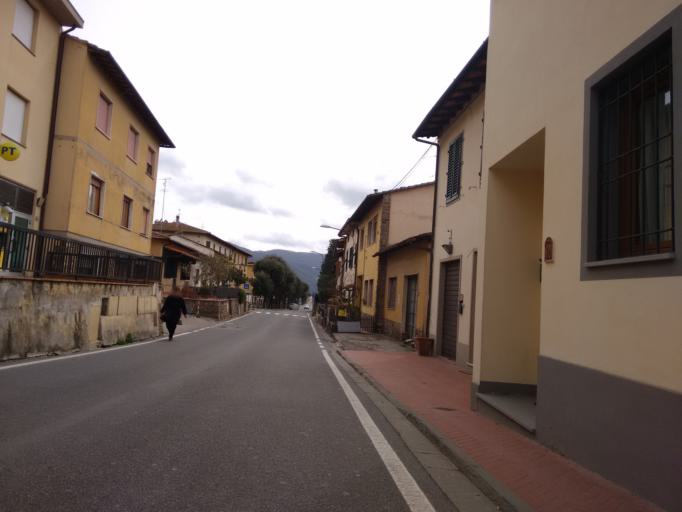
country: IT
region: Tuscany
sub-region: Province of Florence
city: Strada in Chianti
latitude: 43.6581
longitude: 11.2982
